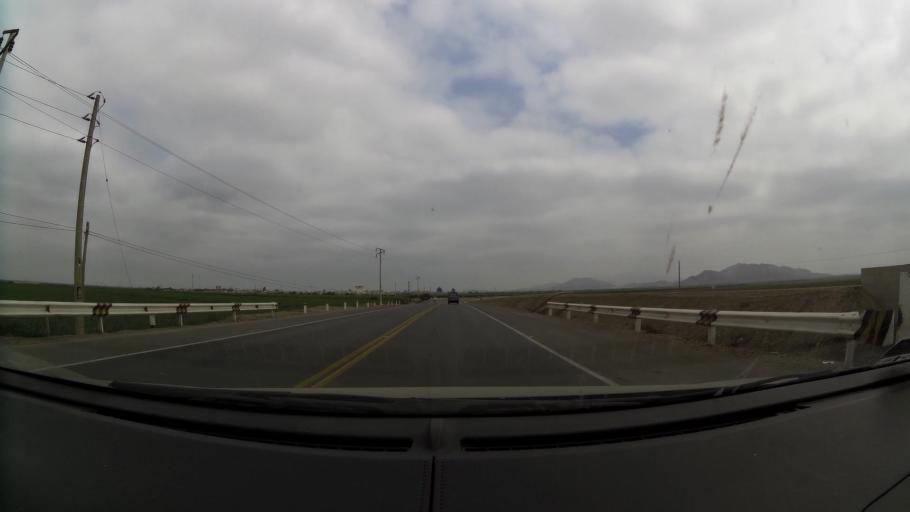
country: PE
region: La Libertad
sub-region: Ascope
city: Chocope
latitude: -7.7942
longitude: -79.2095
